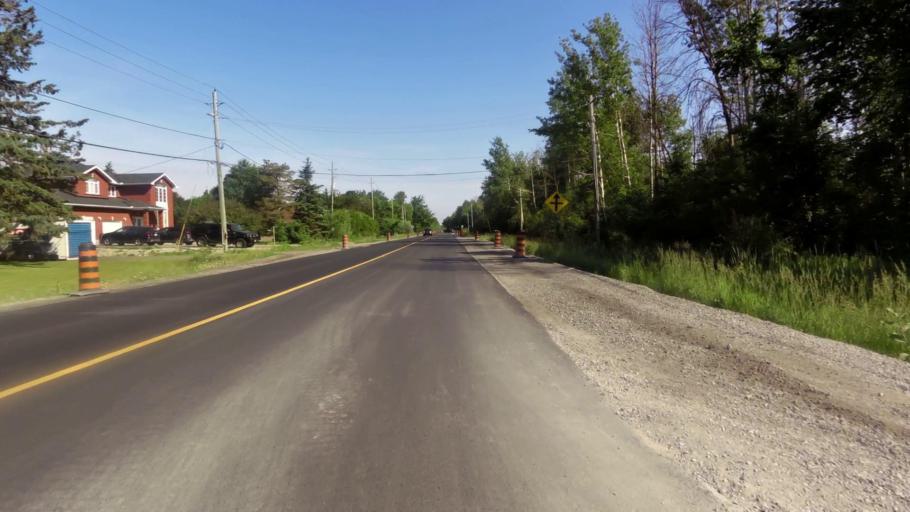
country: CA
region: Ontario
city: Ottawa
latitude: 45.2555
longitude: -75.5934
